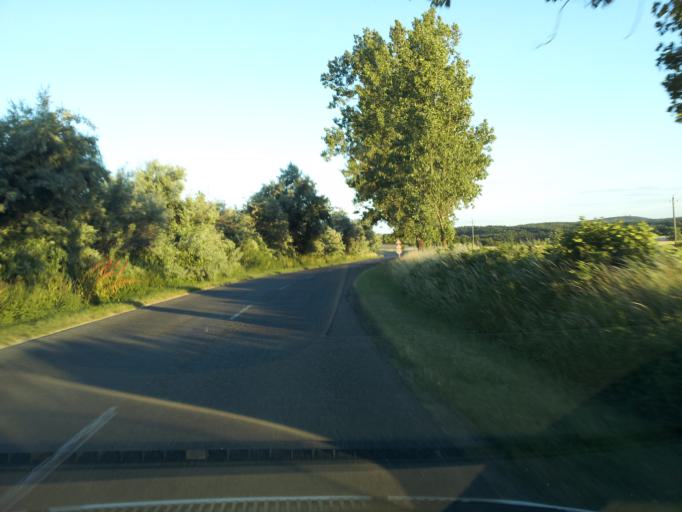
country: HU
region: Veszprem
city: Szentkiralyszabadja
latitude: 47.0344
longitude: 17.9329
